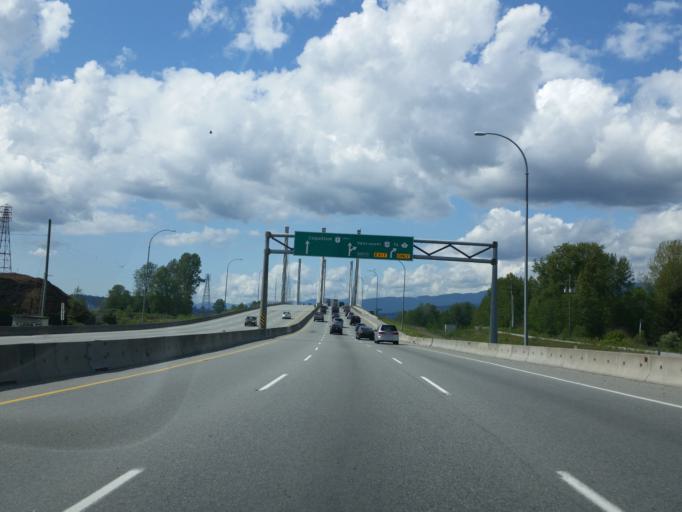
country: CA
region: British Columbia
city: Pitt Meadows
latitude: 49.2456
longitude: -122.7235
